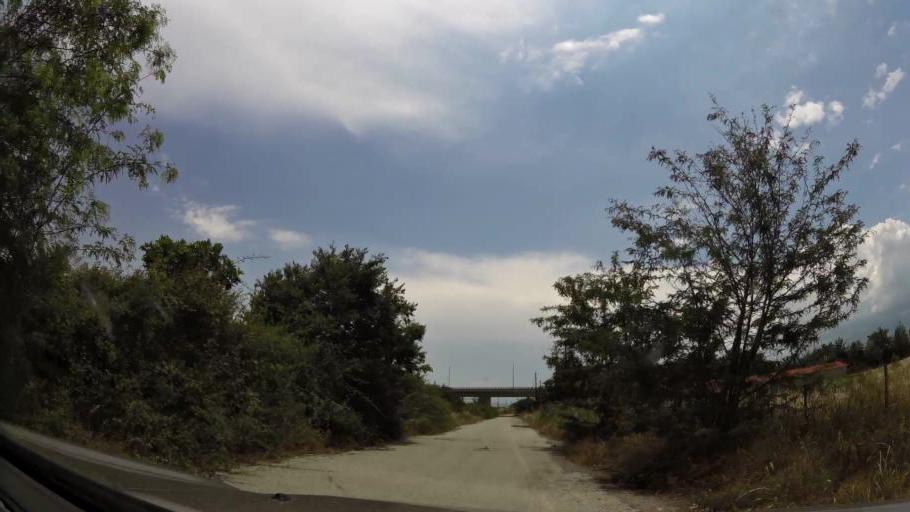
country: GR
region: Central Macedonia
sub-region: Nomos Pierias
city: Peristasi
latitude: 40.2647
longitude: 22.5298
